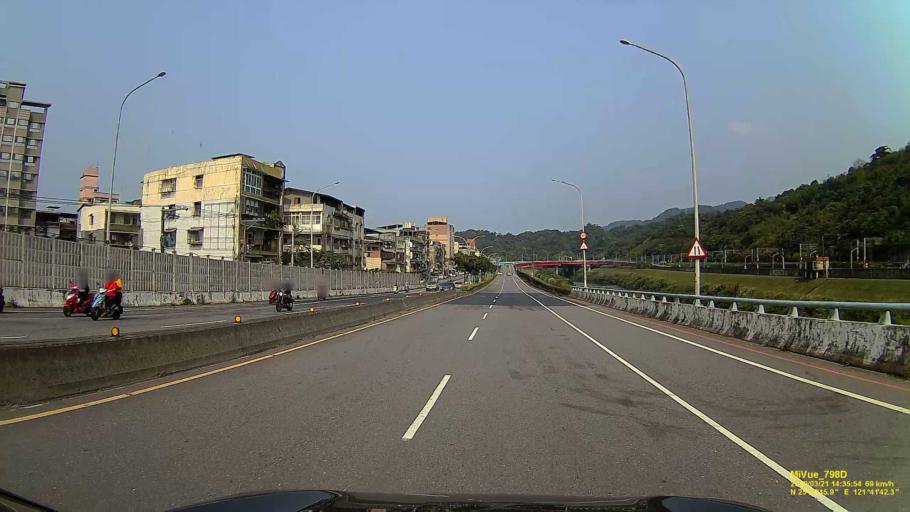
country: TW
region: Taiwan
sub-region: Keelung
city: Keelung
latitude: 25.0795
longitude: 121.6952
